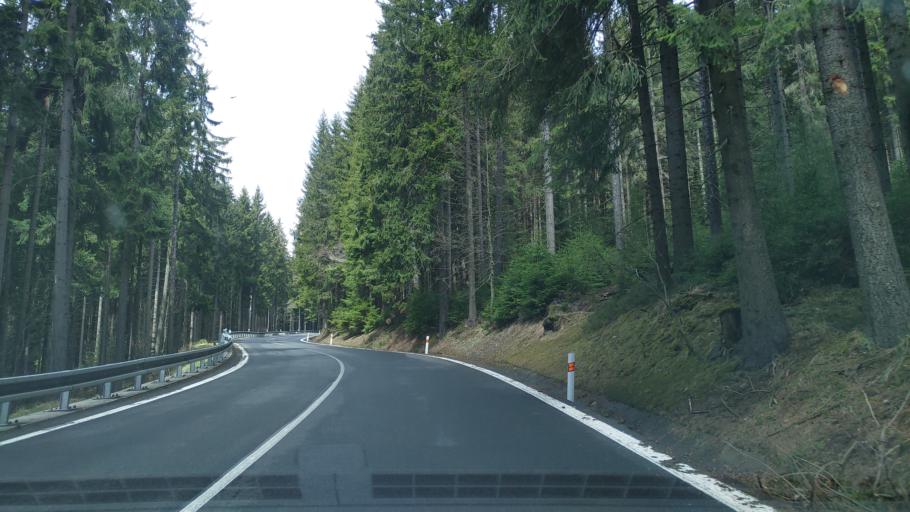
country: CZ
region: Karlovarsky
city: Jachymov
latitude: 50.3842
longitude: 12.9100
